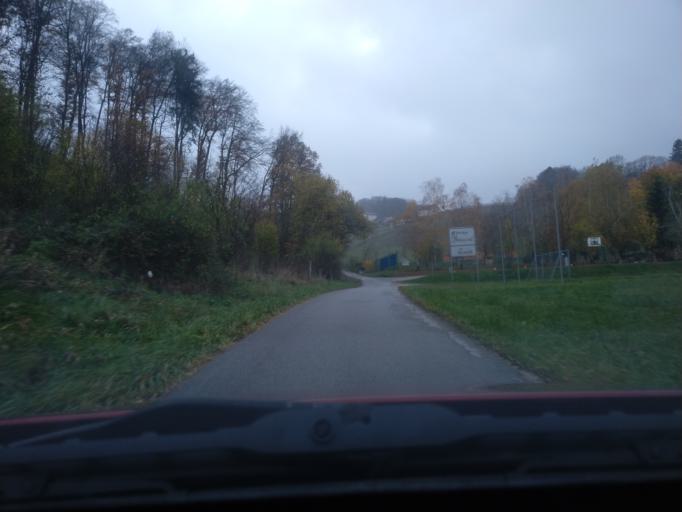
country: SI
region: Pesnica
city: Pesnica pri Mariboru
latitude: 46.5987
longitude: 15.6540
